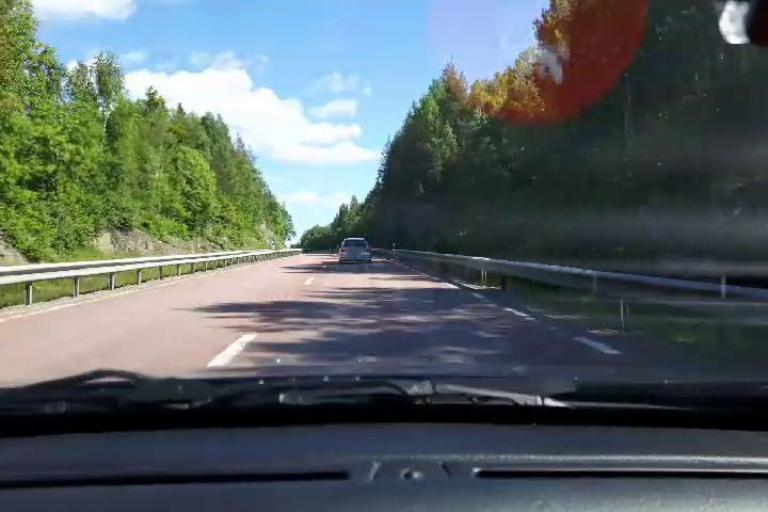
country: SE
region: Gaevleborg
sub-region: Hudiksvalls Kommun
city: Sorforsa
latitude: 61.7412
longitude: 16.8625
